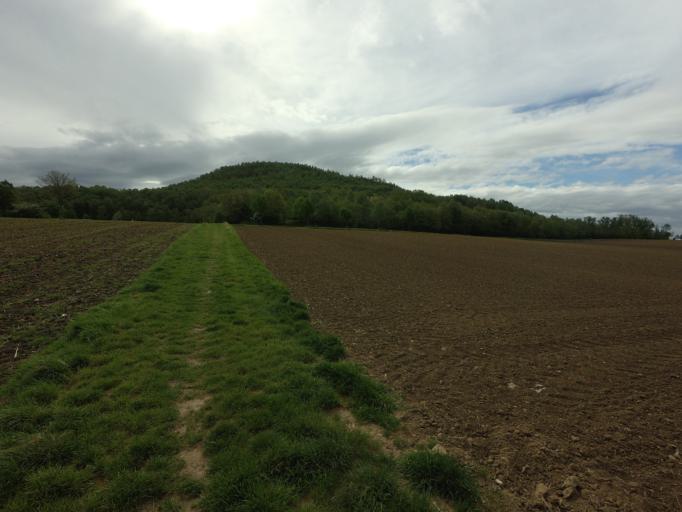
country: DE
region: North Rhine-Westphalia
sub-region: Regierungsbezirk Koln
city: Herzogenrath
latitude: 50.8955
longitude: 6.1065
